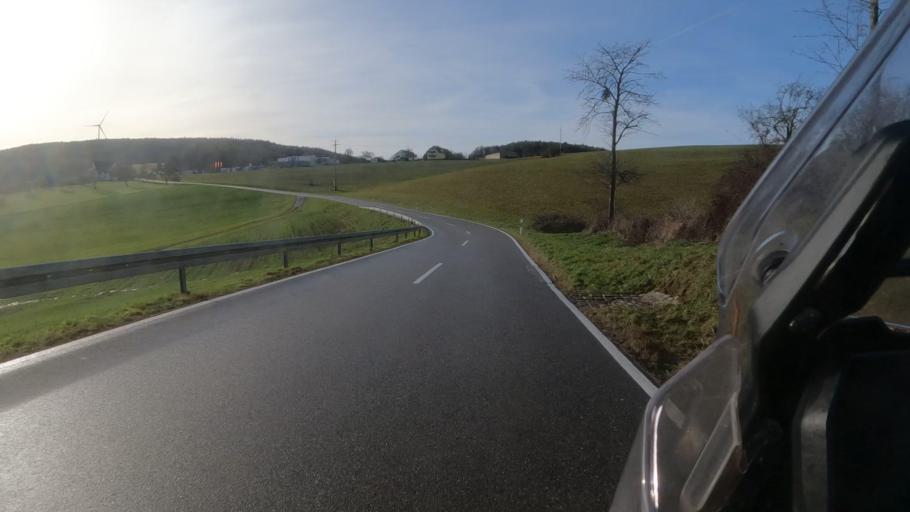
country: DE
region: Baden-Wuerttemberg
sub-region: Freiburg Region
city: Tengen
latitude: 47.7885
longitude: 8.6335
